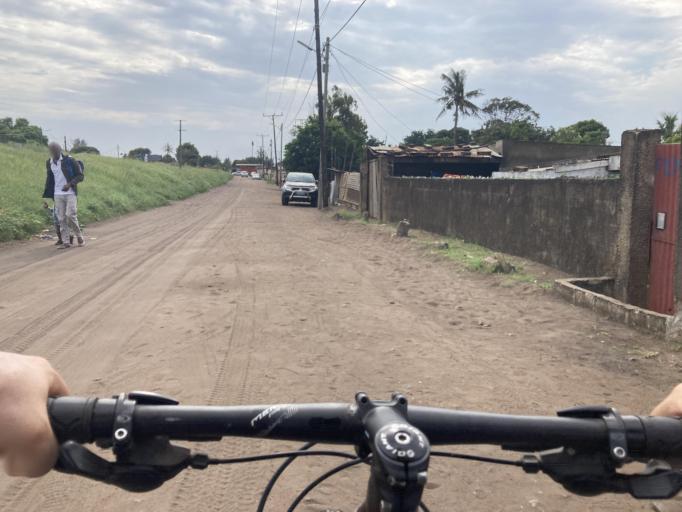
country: MZ
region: Maputo City
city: Maputo
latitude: -25.9268
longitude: 32.5870
